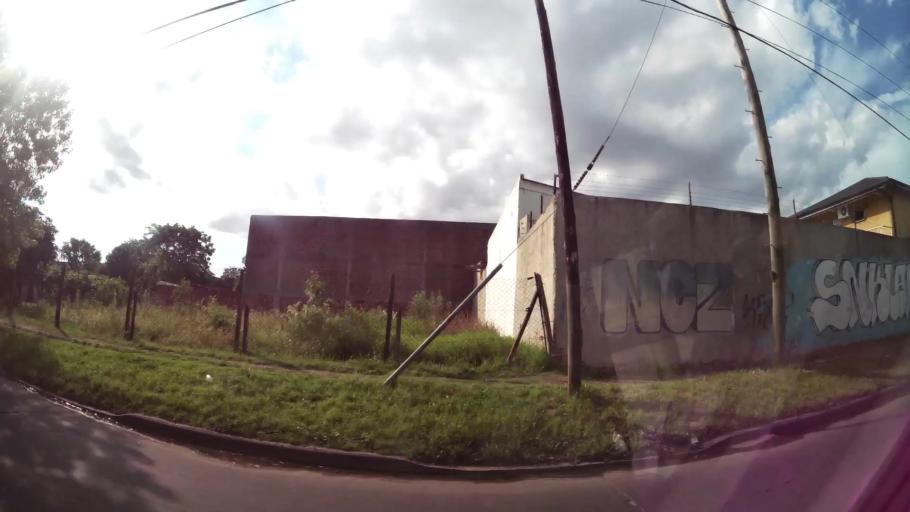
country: AR
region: Buenos Aires
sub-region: Partido de Tigre
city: Tigre
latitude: -34.4700
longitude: -58.6580
